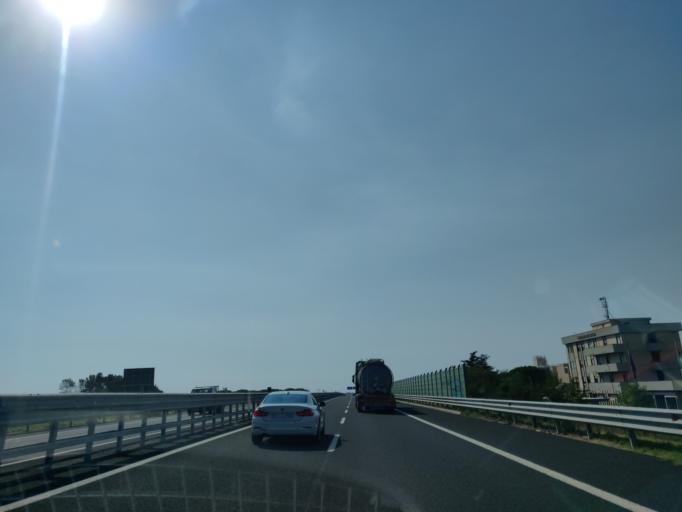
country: IT
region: Latium
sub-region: Provincia di Viterbo
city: Tarquinia
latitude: 42.2417
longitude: 11.7538
